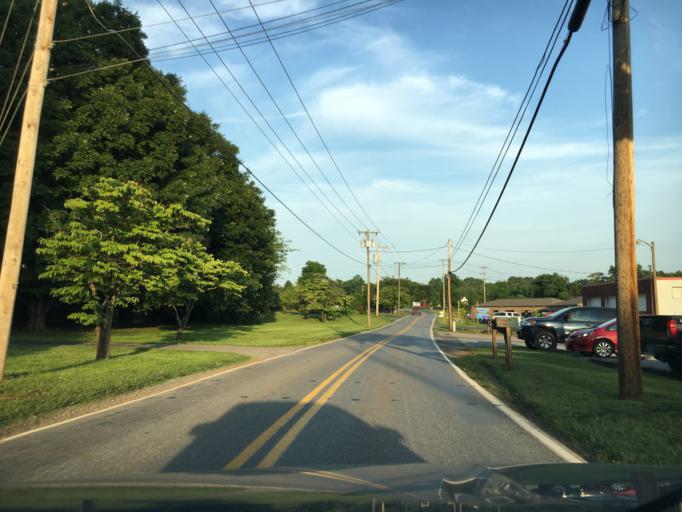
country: US
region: Virginia
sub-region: Bedford County
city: Forest
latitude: 37.3627
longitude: -79.2881
